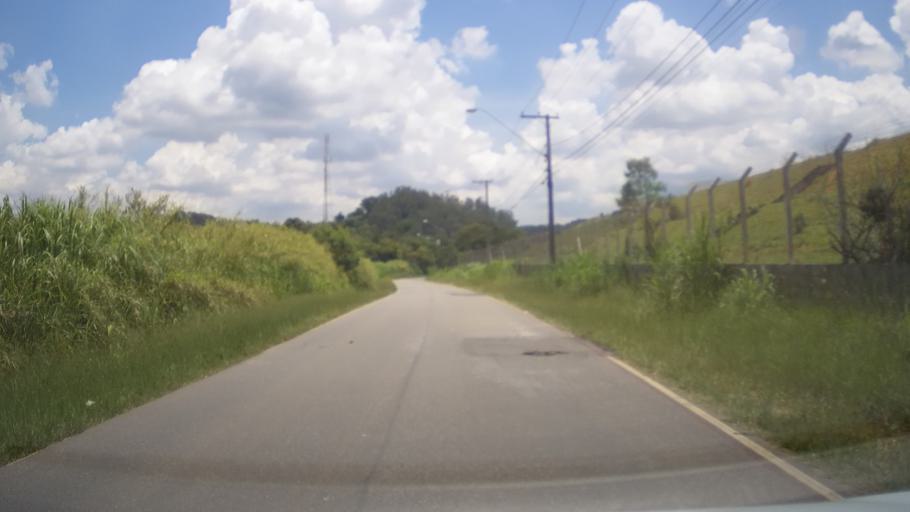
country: BR
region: Sao Paulo
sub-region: Vinhedo
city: Vinhedo
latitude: -23.0622
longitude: -47.0368
